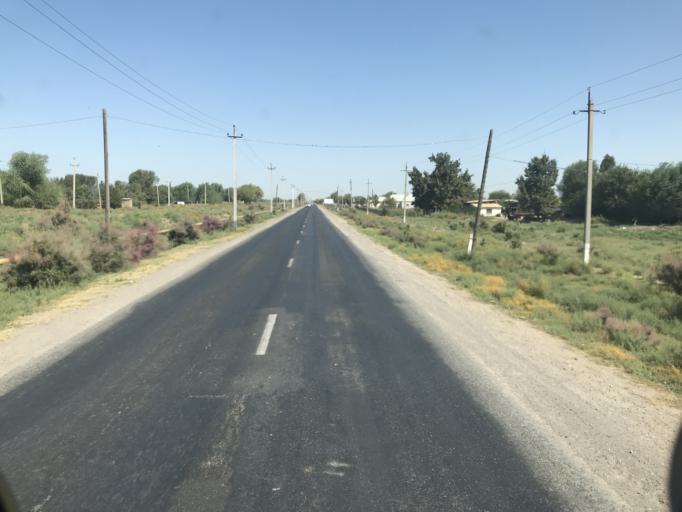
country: KZ
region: Ongtustik Qazaqstan
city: Ilyich
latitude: 40.8926
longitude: 68.4882
